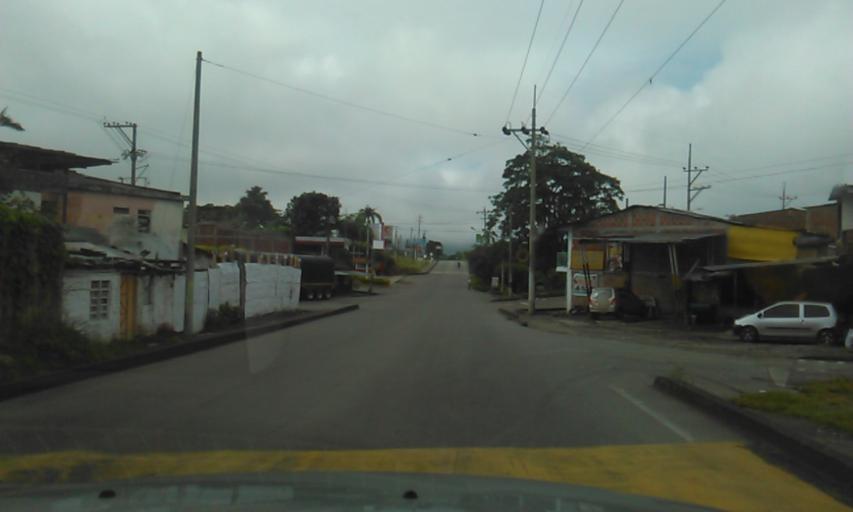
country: CO
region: Quindio
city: Cordoba
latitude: 4.4271
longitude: -75.7201
